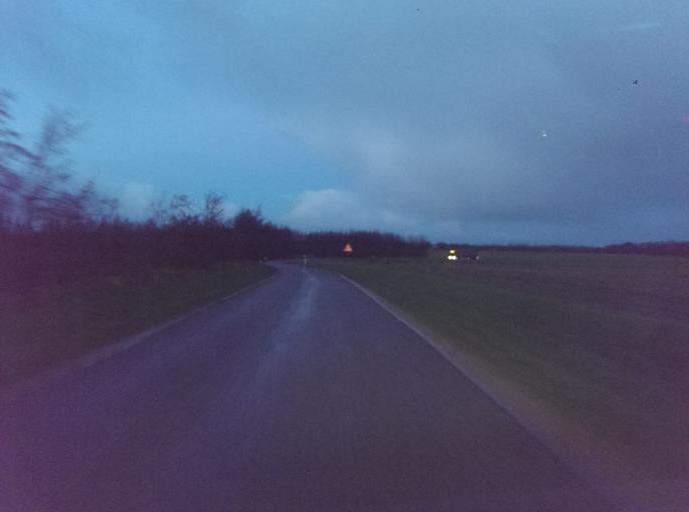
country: DK
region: South Denmark
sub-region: Esbjerg Kommune
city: Bramming
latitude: 55.4471
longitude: 8.6483
